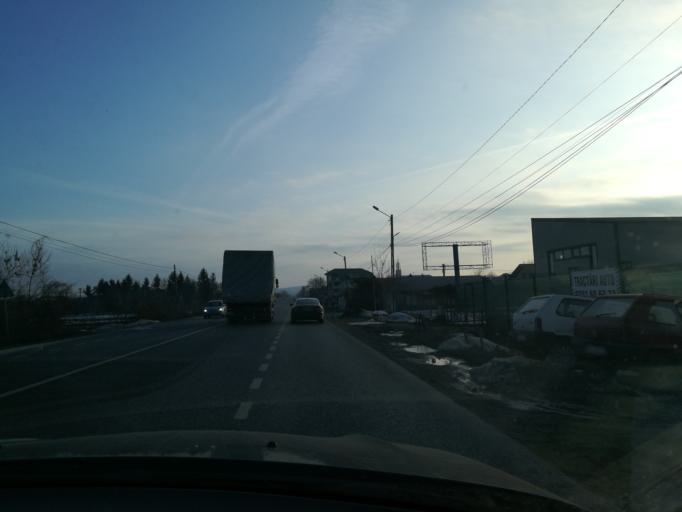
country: RO
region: Bacau
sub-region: Comuna Nicolae Balcescu
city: Nicolae Balcescu
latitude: 46.4859
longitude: 26.9211
